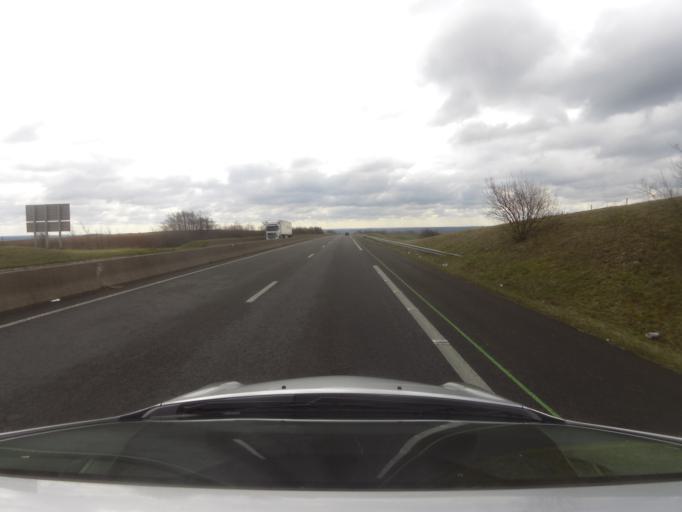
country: FR
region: Nord-Pas-de-Calais
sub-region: Departement du Pas-de-Calais
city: Etaples
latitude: 50.5580
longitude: 1.6668
